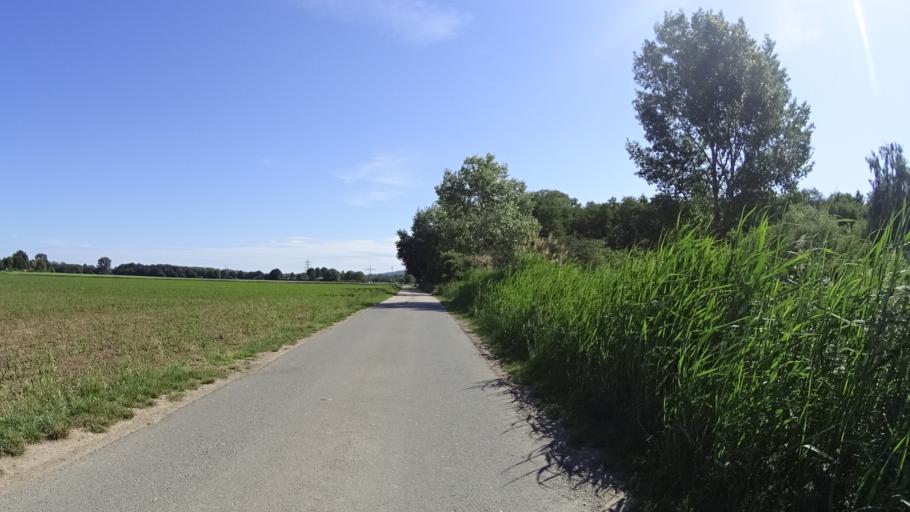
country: DE
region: Hesse
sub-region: Regierungsbezirk Darmstadt
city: Alsbach-Hahnlein
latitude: 49.7556
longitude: 8.5862
